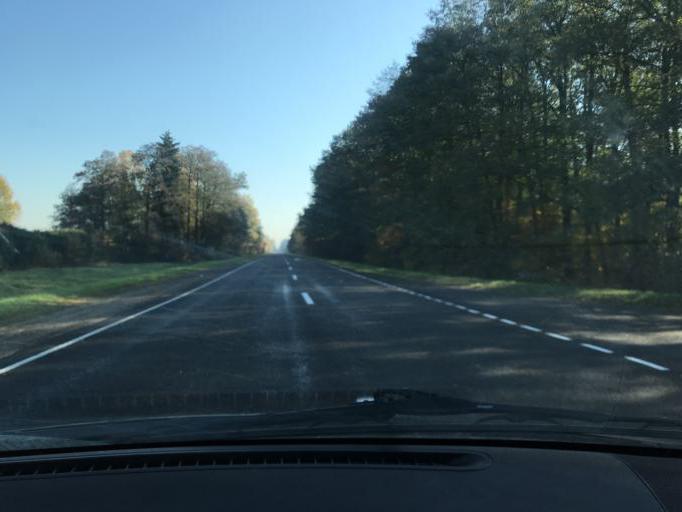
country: BY
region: Brest
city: Lyakhavichy
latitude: 52.9517
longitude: 26.1946
